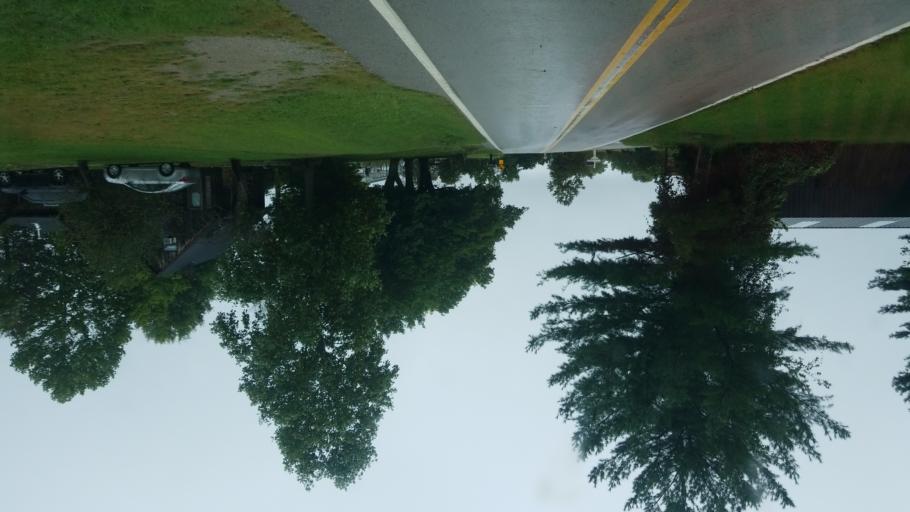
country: US
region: Ohio
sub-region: Adams County
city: West Union
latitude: 38.7344
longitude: -83.5169
